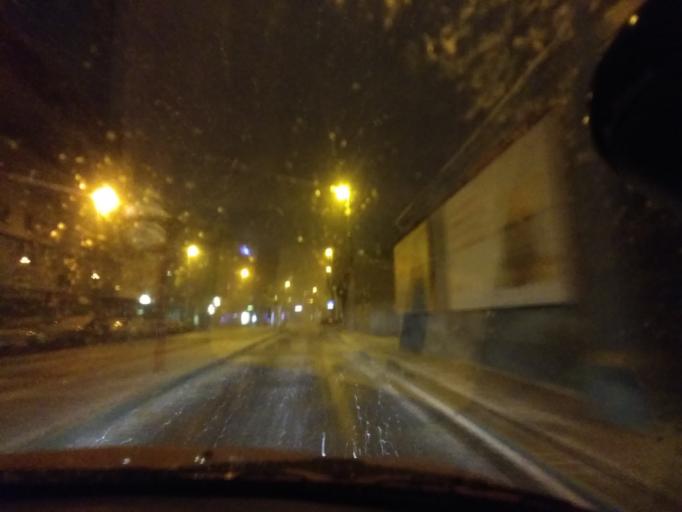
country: AT
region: Lower Austria
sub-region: Politischer Bezirk Wien-Umgebung
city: Gerasdorf bei Wien
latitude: 48.2531
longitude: 16.4202
